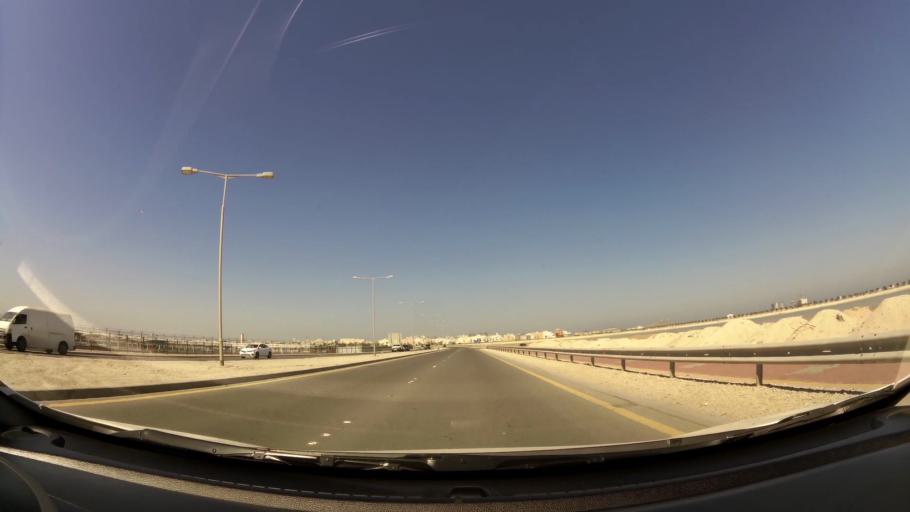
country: BH
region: Muharraq
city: Al Hadd
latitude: 26.2564
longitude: 50.6554
